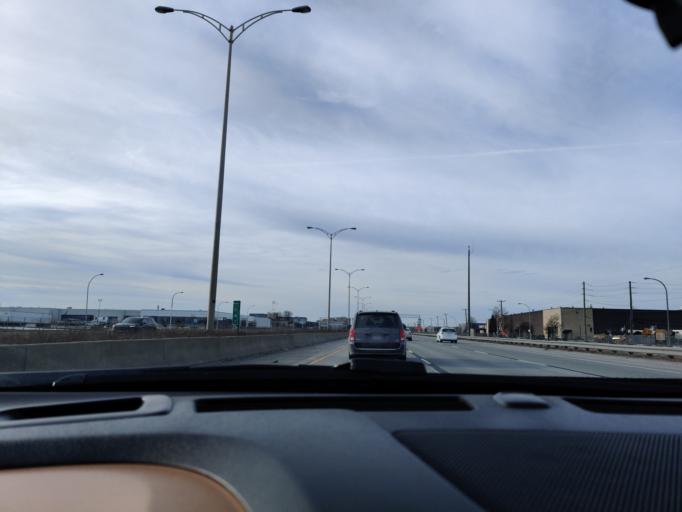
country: CA
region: Quebec
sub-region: Montreal
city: Pointe-Claire
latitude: 45.4727
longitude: -73.8087
